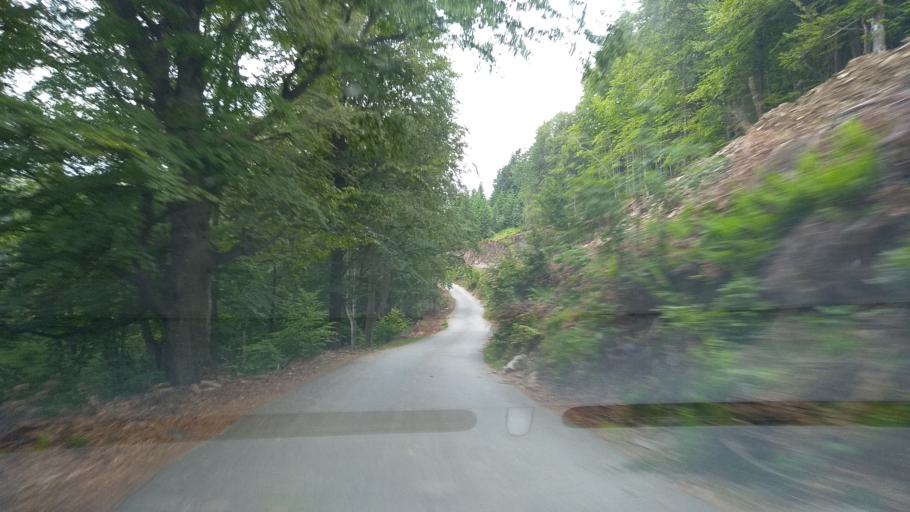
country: RO
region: Hunedoara
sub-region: Municipiul  Vulcan
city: Jiu-Paroseni
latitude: 45.3222
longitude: 23.2941
